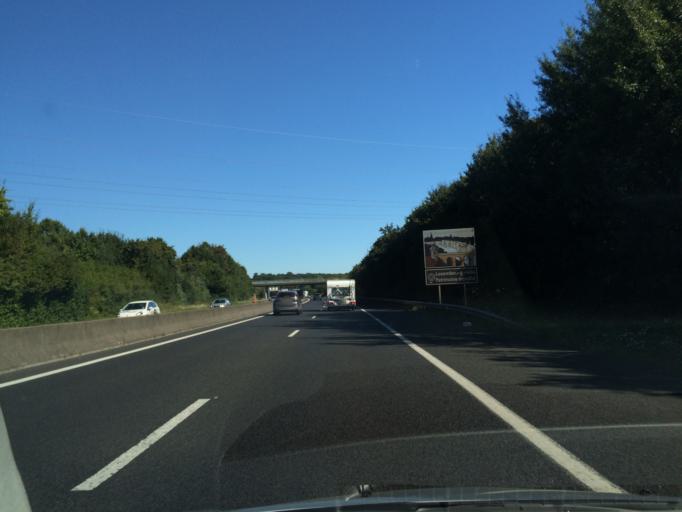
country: LU
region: Luxembourg
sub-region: Canton d'Esch-sur-Alzette
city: Roeser
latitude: 49.5523
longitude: 6.1282
